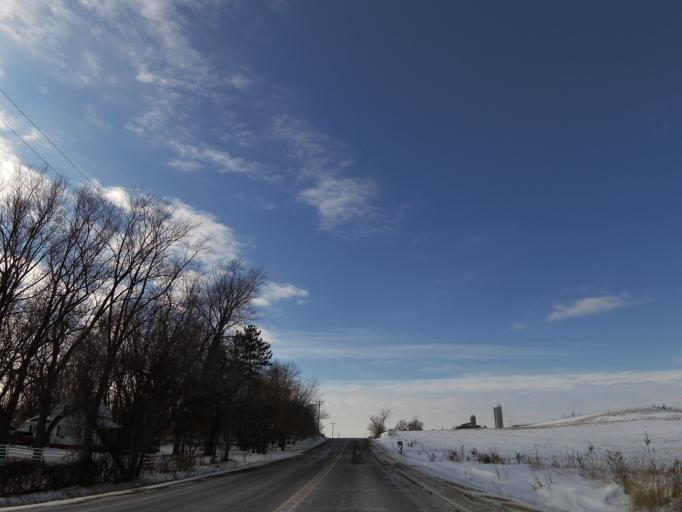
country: US
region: Wisconsin
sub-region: Saint Croix County
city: Roberts
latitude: 44.9926
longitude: -92.5911
